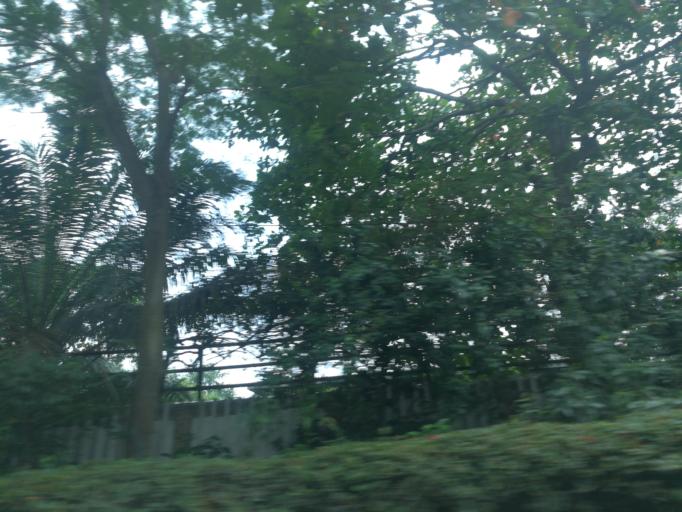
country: NG
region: Lagos
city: Oshodi
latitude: 6.5741
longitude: 3.3560
